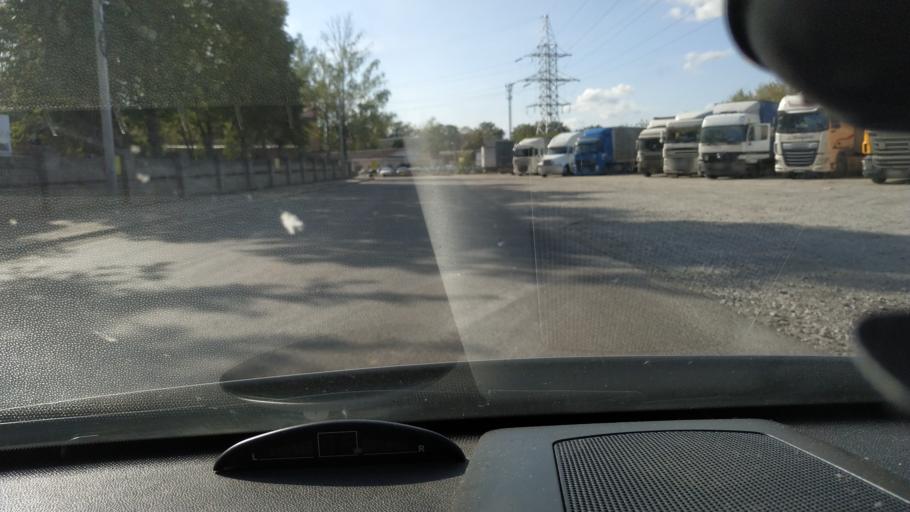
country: RU
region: Rjazan
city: Ryazan'
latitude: 54.6694
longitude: 39.6215
